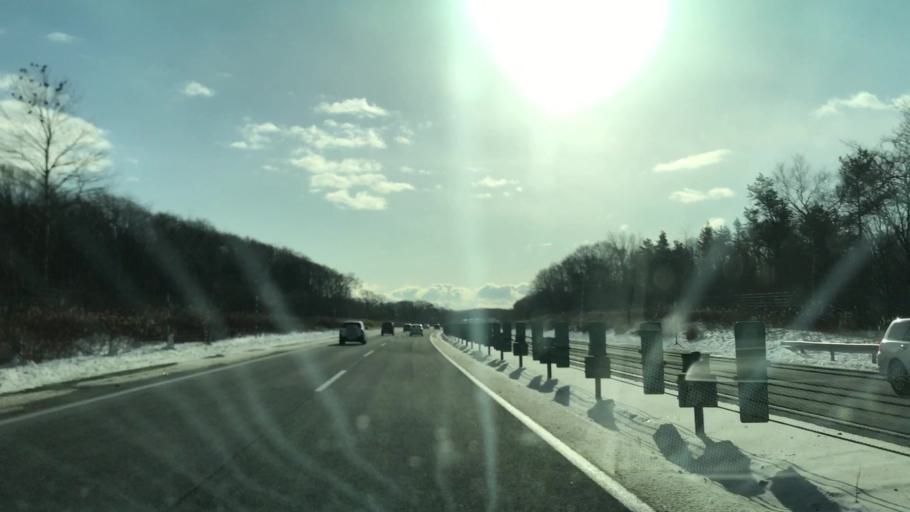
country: JP
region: Hokkaido
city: Chitose
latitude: 42.8329
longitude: 141.6100
